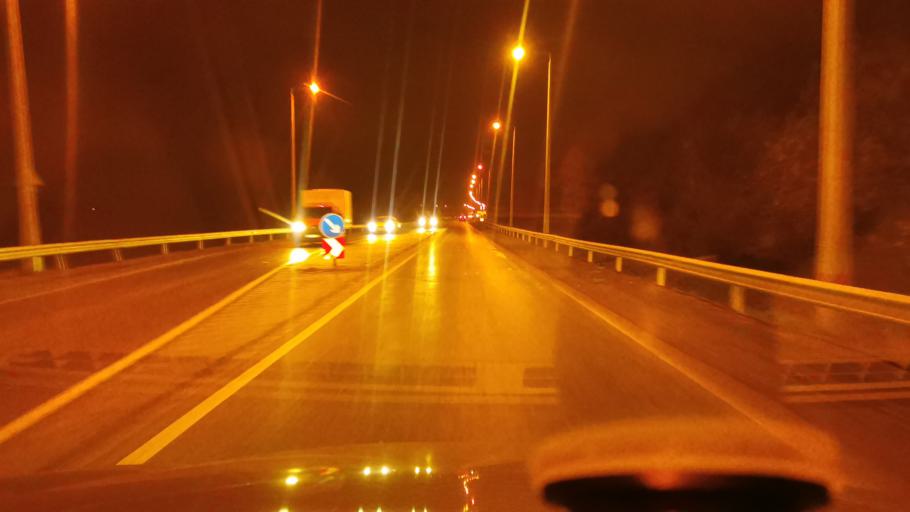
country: HU
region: Hajdu-Bihar
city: Debrecen
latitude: 47.5942
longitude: 21.5797
